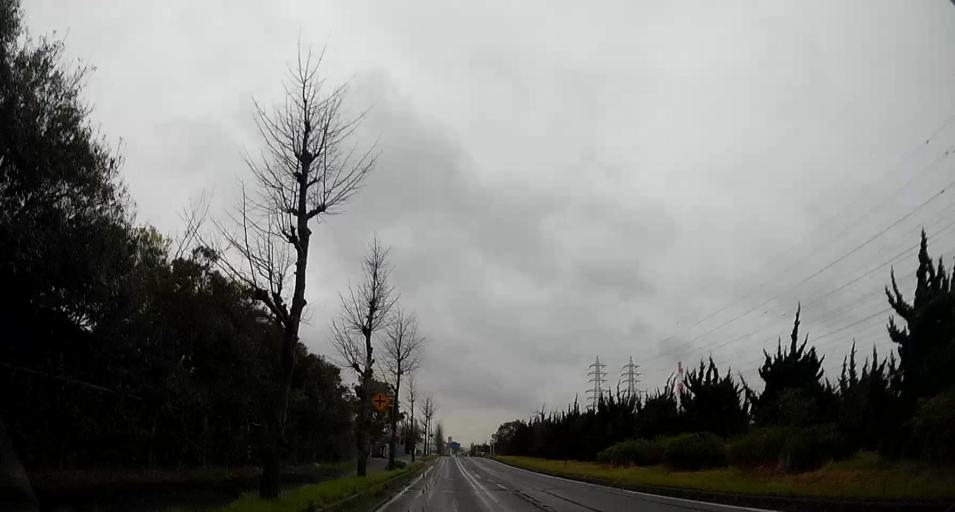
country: JP
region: Chiba
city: Ichihara
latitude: 35.4924
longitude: 140.0443
